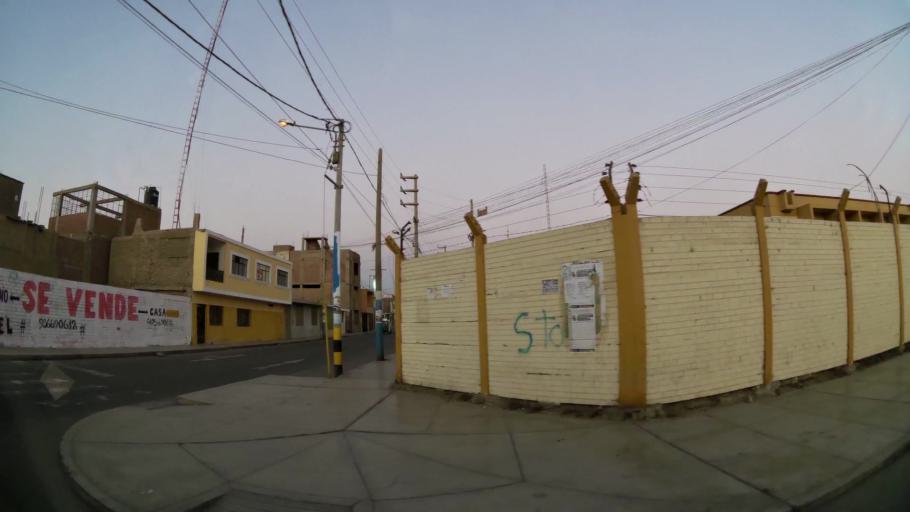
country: PE
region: Ica
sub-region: Provincia de Pisco
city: Pisco
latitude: -13.7074
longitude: -76.2023
